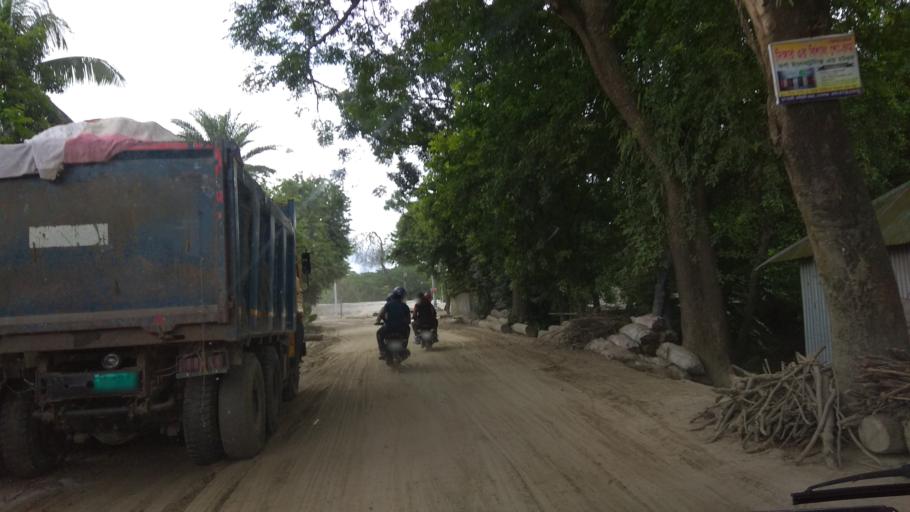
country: BD
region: Khulna
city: Kalia
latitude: 23.1960
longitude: 89.6961
